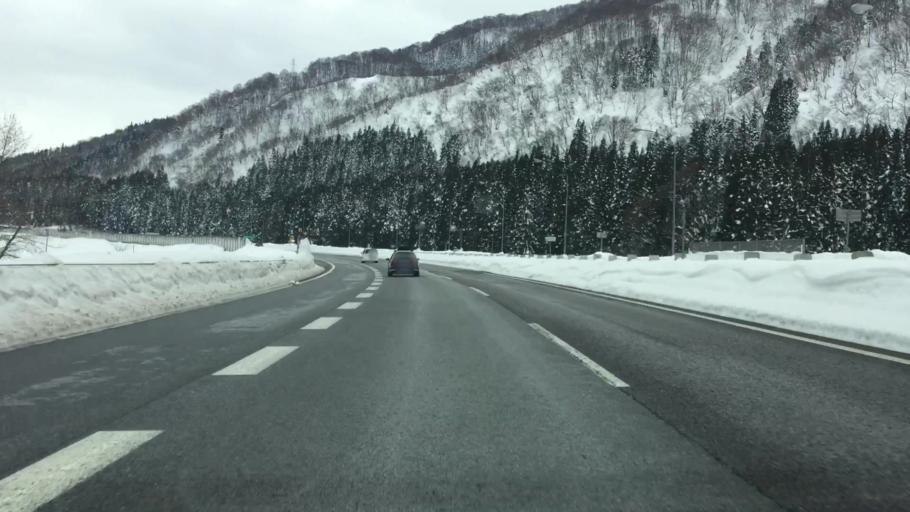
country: JP
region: Niigata
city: Shiozawa
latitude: 36.8972
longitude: 138.8455
